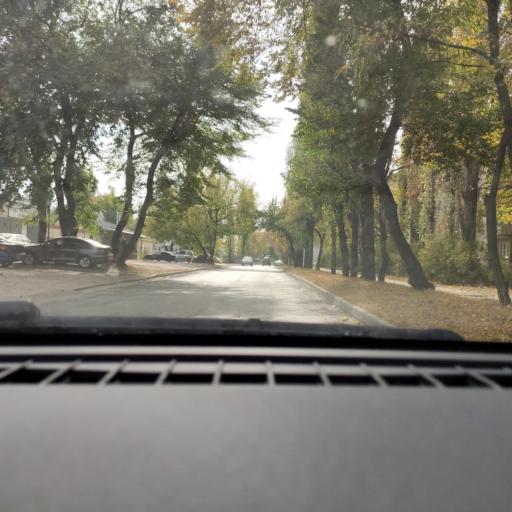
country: RU
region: Voronezj
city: Voronezh
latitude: 51.6808
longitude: 39.2704
